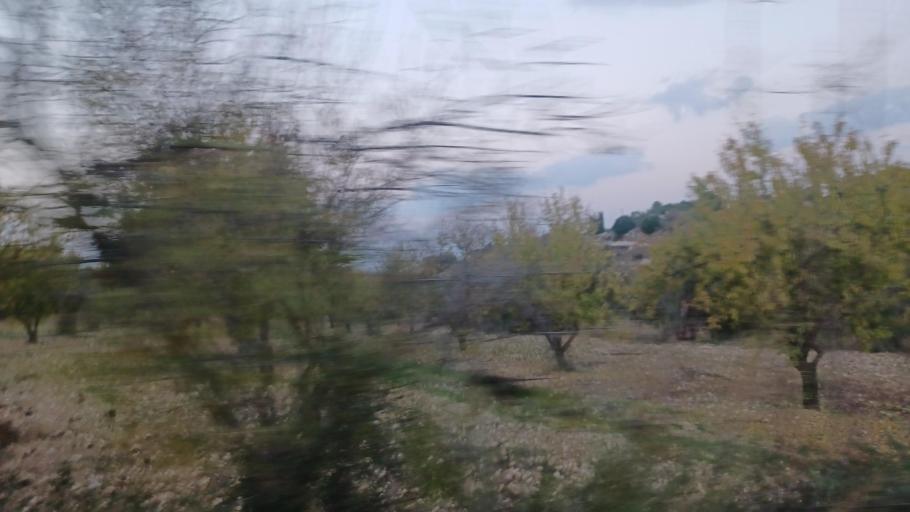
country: CY
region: Pafos
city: Tala
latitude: 34.9353
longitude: 32.5116
